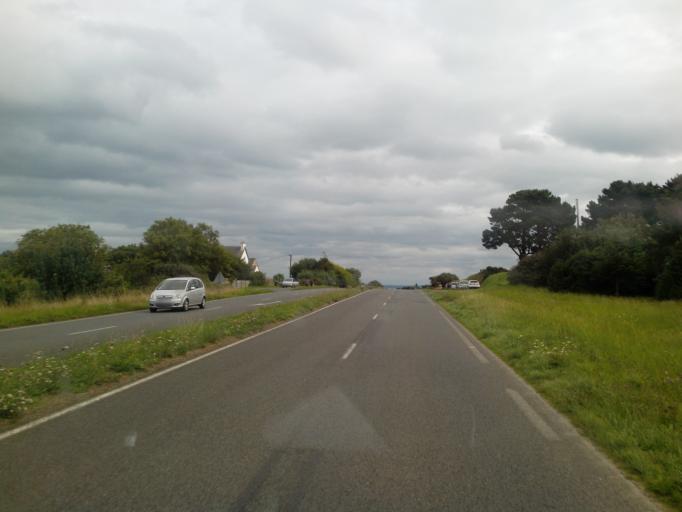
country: FR
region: Brittany
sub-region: Departement des Cotes-d'Armor
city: Saint-Quay-Portrieux
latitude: 48.6522
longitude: -2.8442
